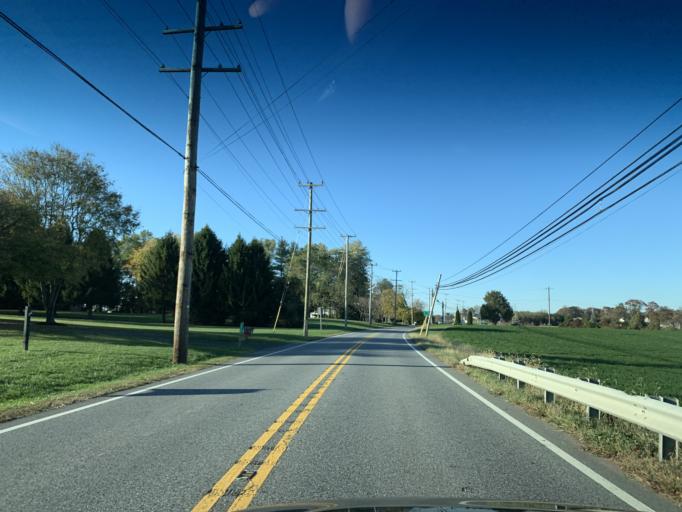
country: US
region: Maryland
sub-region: Harford County
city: Jarrettsville
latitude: 39.5847
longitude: -76.4718
